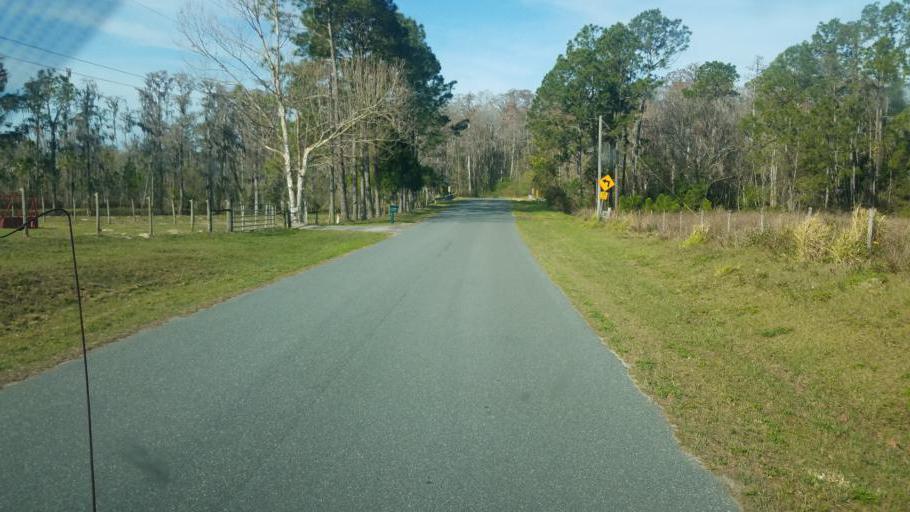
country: US
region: Florida
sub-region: Lake County
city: Clermont
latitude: 28.4487
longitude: -81.7801
